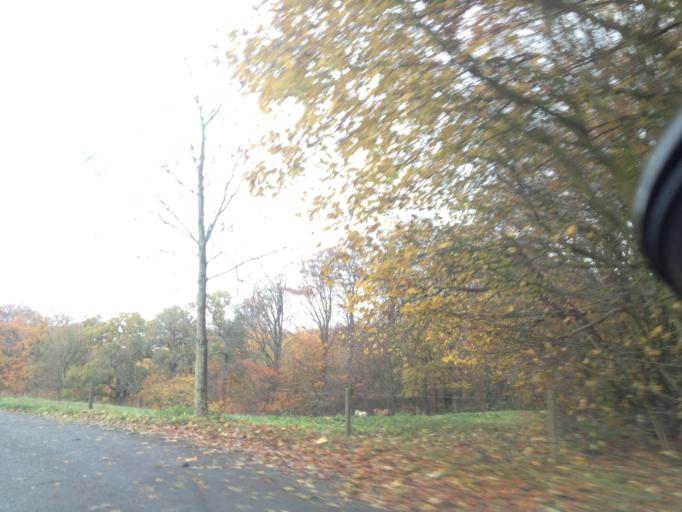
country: DK
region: South Denmark
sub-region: Assens Kommune
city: Vissenbjerg
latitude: 55.4269
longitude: 10.1685
